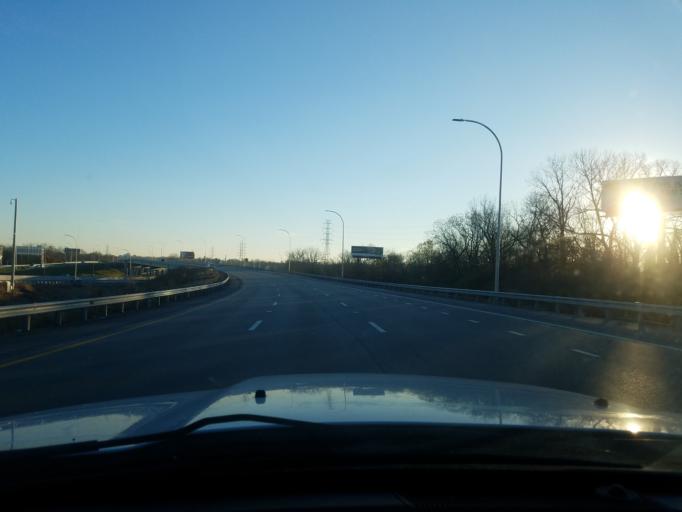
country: US
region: Indiana
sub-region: Clark County
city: Jeffersonville
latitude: 38.2606
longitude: -85.7315
